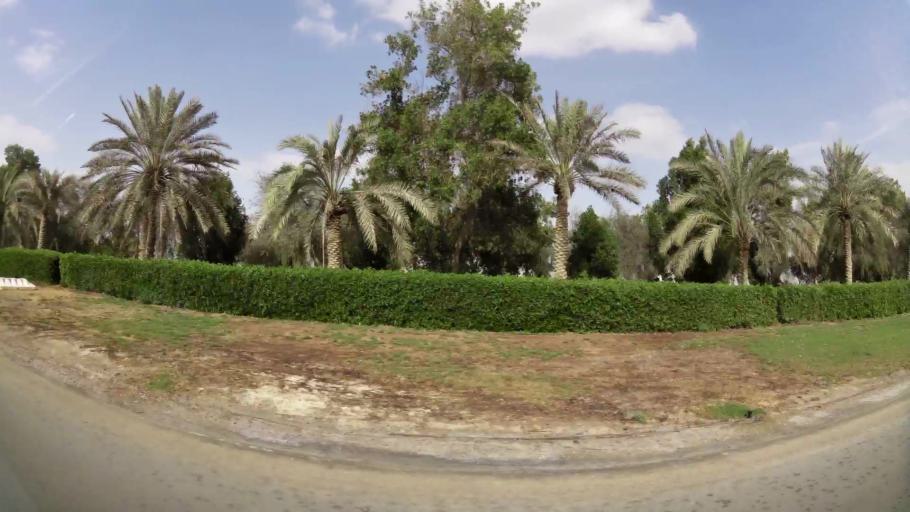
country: AE
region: Abu Dhabi
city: Abu Dhabi
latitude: 24.3942
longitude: 54.5357
